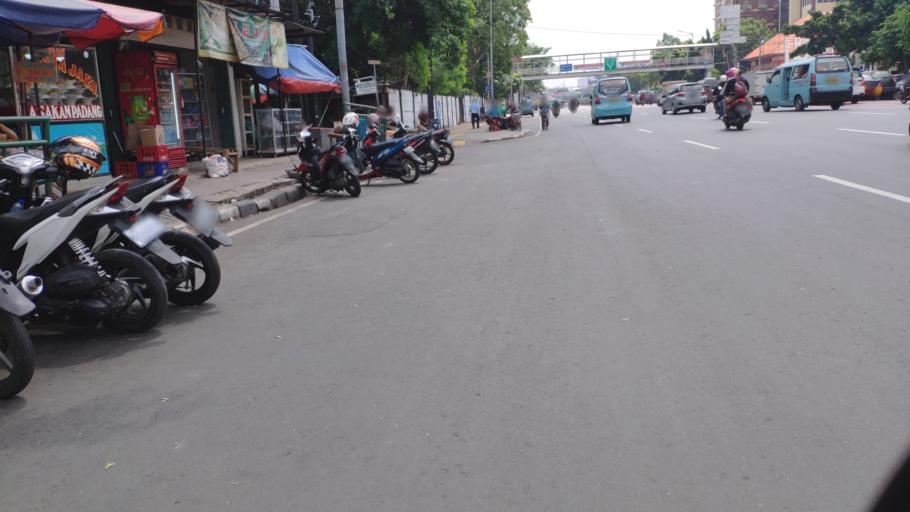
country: ID
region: Jakarta Raya
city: Jakarta
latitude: -6.2134
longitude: 106.8619
